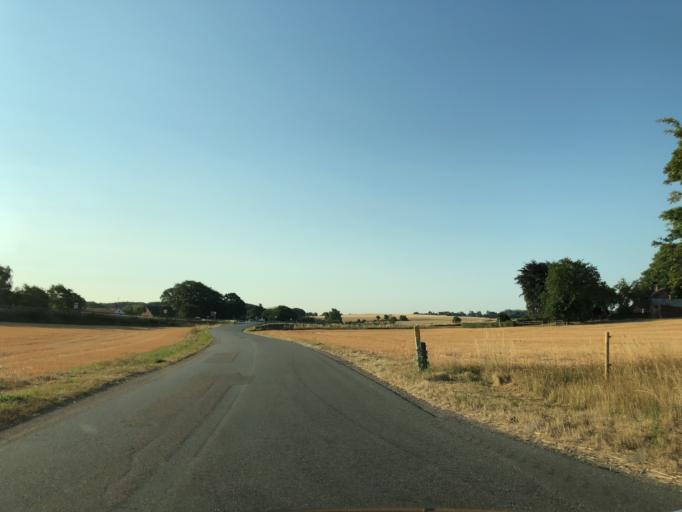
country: DK
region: Central Jutland
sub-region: Skanderborg Kommune
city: Stilling
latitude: 56.0928
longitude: 9.9671
